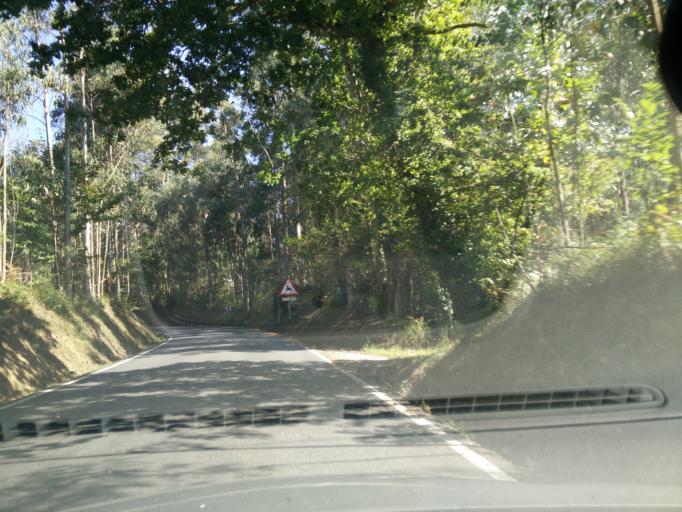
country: ES
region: Galicia
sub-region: Provincia da Coruna
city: Mino
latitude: 43.3397
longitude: -8.1489
